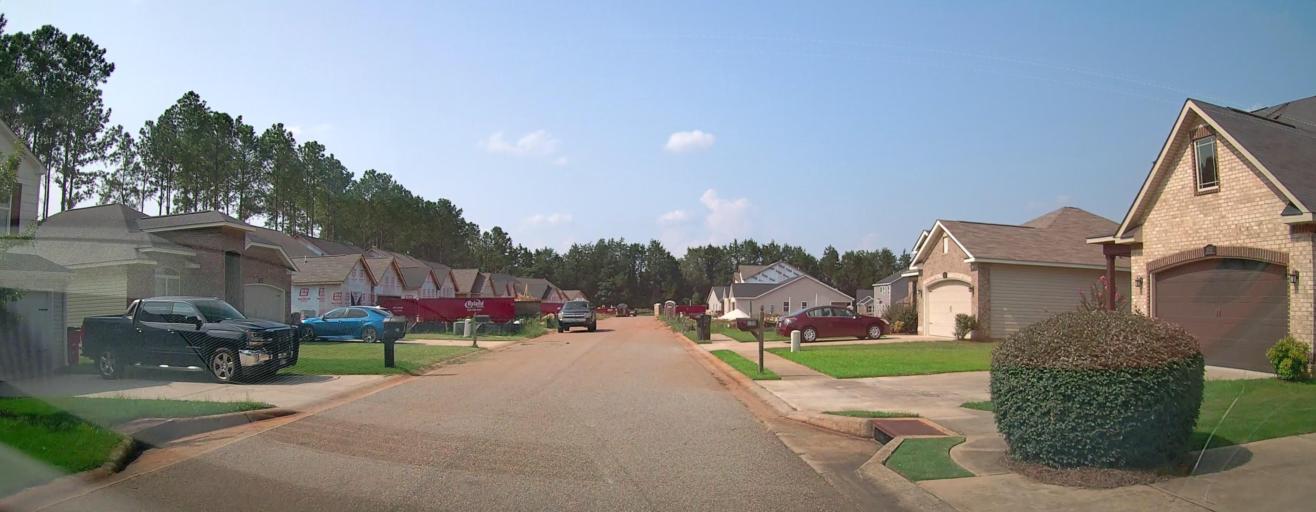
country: US
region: Georgia
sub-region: Houston County
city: Centerville
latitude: 32.6515
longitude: -83.7043
